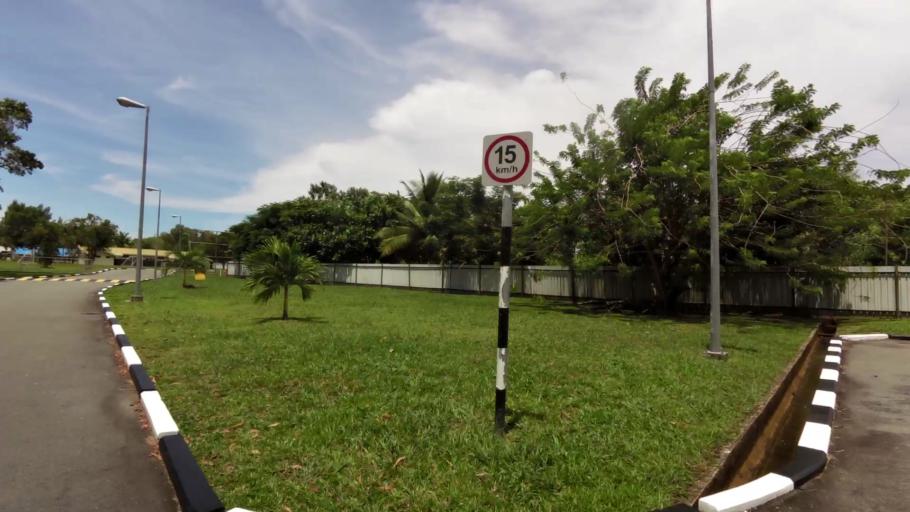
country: BN
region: Belait
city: Kuala Belait
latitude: 4.5945
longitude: 114.2538
